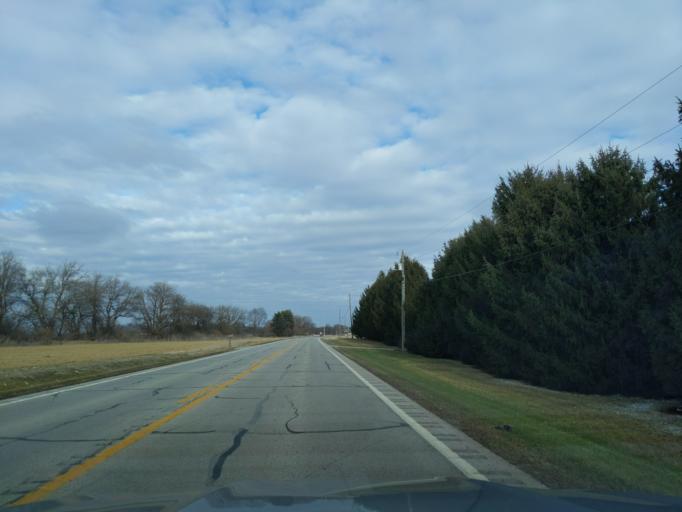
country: US
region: Indiana
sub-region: Tippecanoe County
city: Shadeland
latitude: 40.3669
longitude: -86.9605
